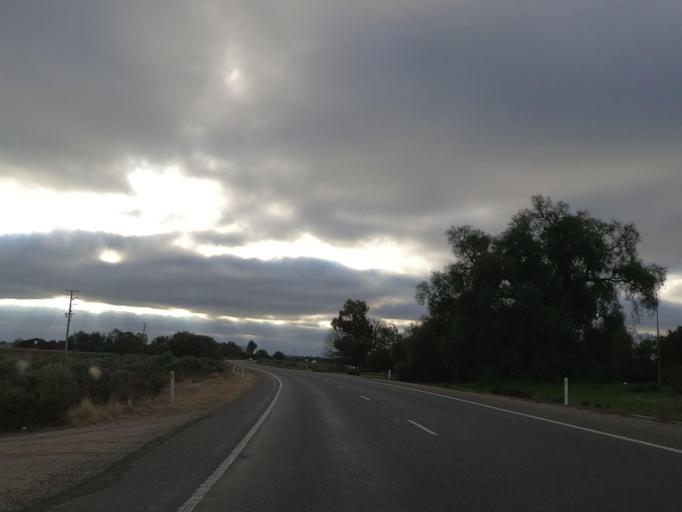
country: AU
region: Victoria
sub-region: Swan Hill
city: Swan Hill
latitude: -35.7239
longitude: 143.8895
